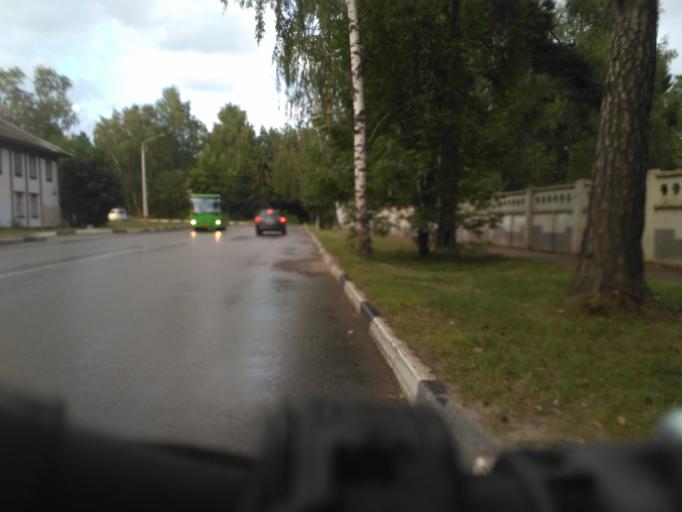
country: RU
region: Moskovskaya
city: Dubna
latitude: 56.7415
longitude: 37.1769
